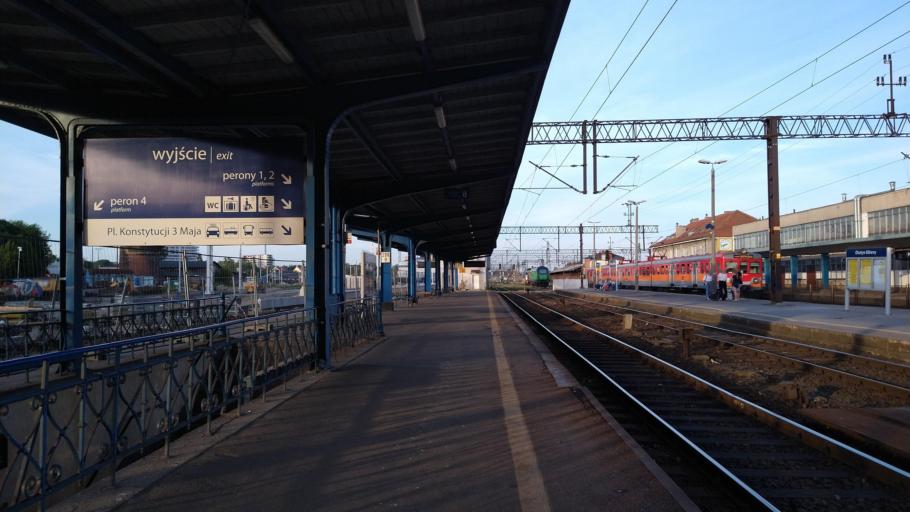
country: PL
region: Warmian-Masurian Voivodeship
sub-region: Powiat olsztynski
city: Olsztyn
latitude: 53.7859
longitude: 20.4972
